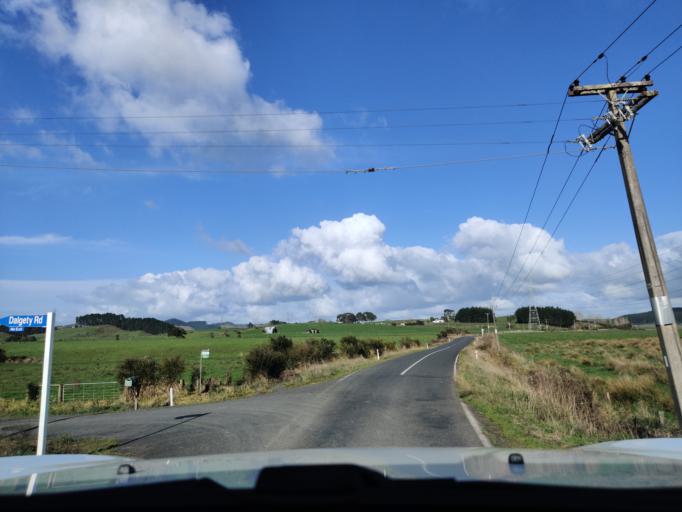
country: NZ
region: Waikato
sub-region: Waikato District
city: Te Kauwhata
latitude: -37.2624
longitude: 175.1950
